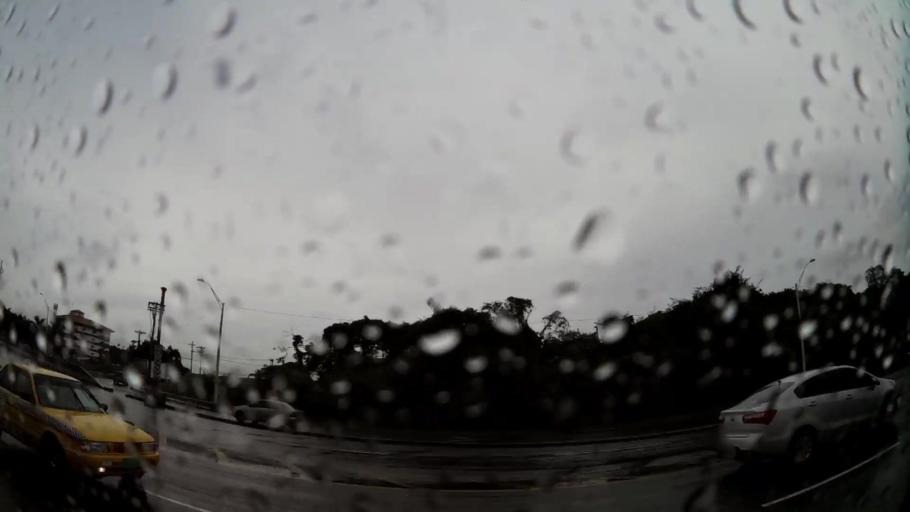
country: PA
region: Colon
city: Arco Iris
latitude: 9.3366
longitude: -79.8866
